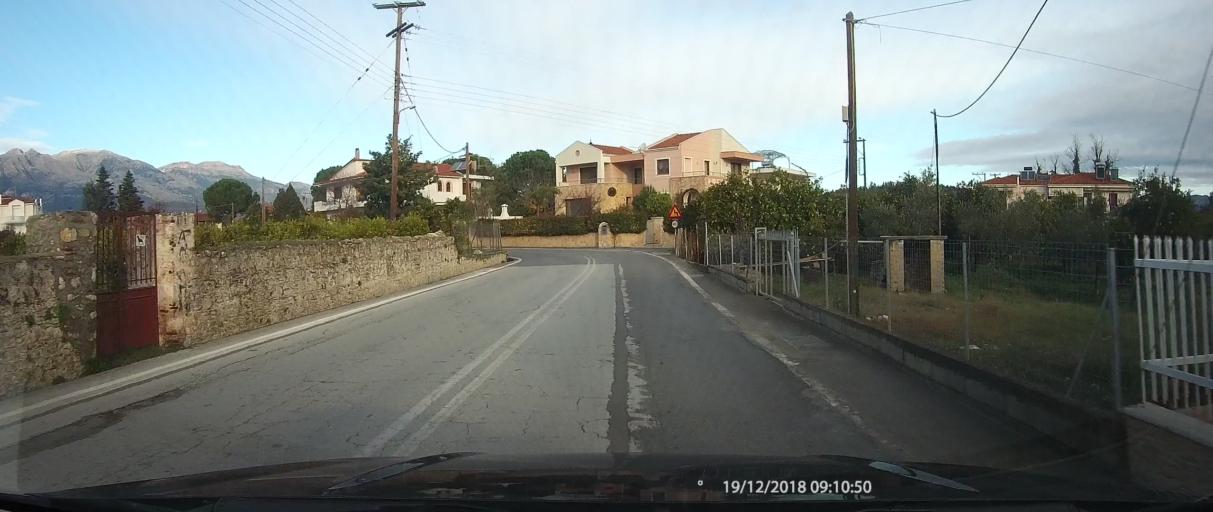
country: GR
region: Peloponnese
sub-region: Nomos Lakonias
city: Sparti
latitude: 37.0770
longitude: 22.4195
